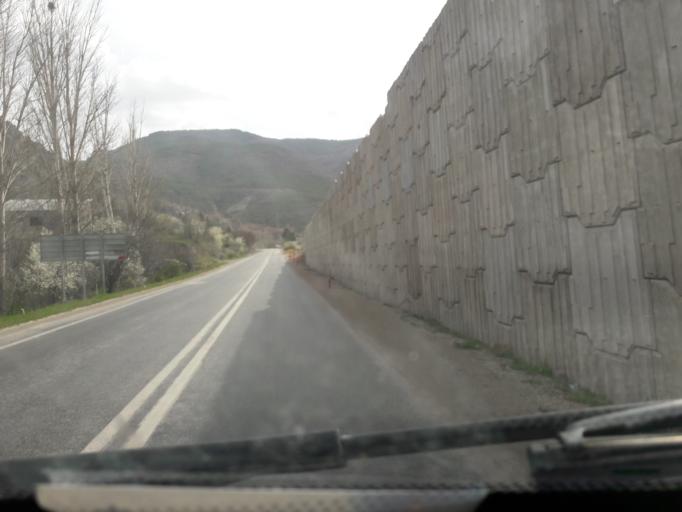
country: TR
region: Gumushane
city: Kale
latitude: 40.4042
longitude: 39.6073
